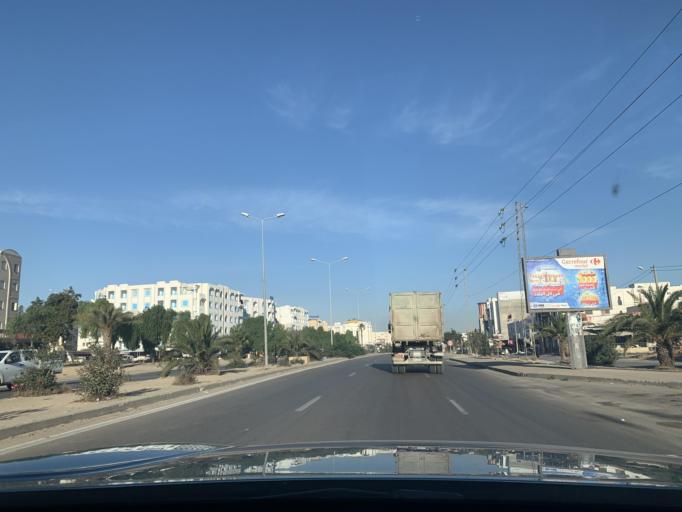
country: DZ
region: Souk Ahras
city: Souk Ahras
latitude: 36.3697
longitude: 7.9979
